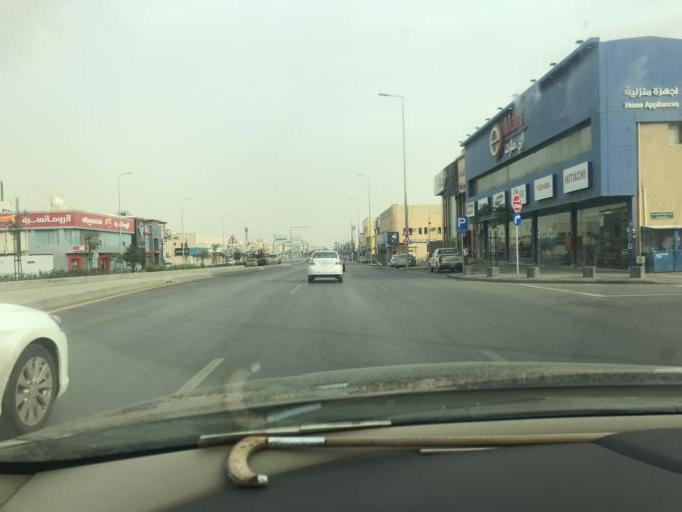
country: SA
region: Ar Riyad
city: Riyadh
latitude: 24.7454
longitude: 46.7756
